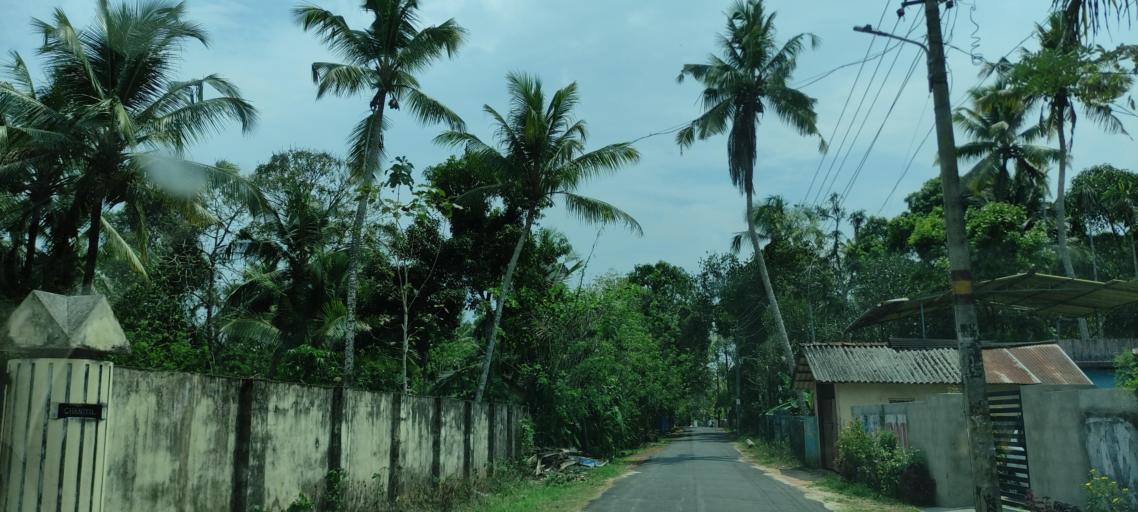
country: IN
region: Kerala
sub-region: Alappuzha
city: Vayalar
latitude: 9.7158
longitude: 76.3408
